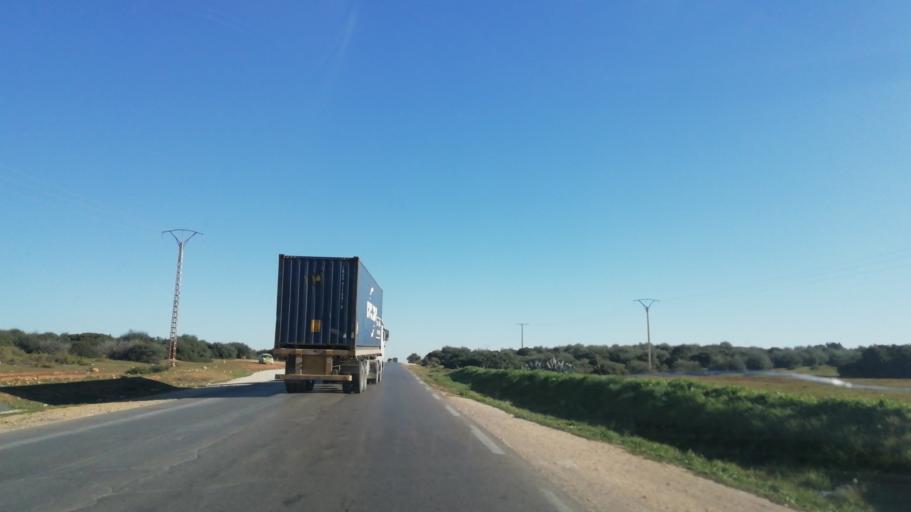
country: DZ
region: Relizane
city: Smala
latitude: 35.6917
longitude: 0.7889
